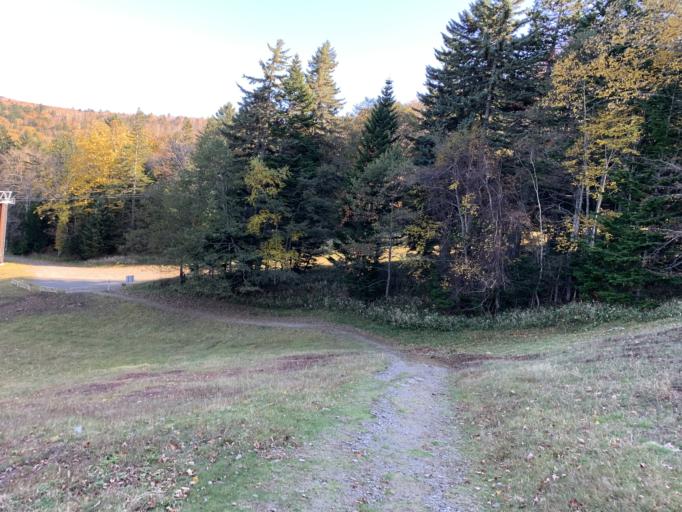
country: JP
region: Hokkaido
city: Bihoro
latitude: 43.4226
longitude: 144.0808
